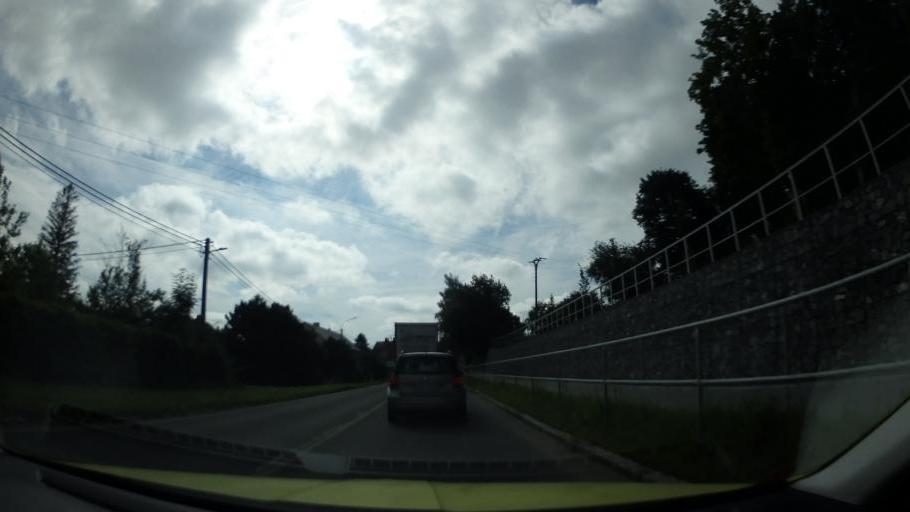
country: CZ
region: Moravskoslezsky
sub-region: Okres Novy Jicin
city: Novy Jicin
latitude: 49.5873
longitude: 18.0208
